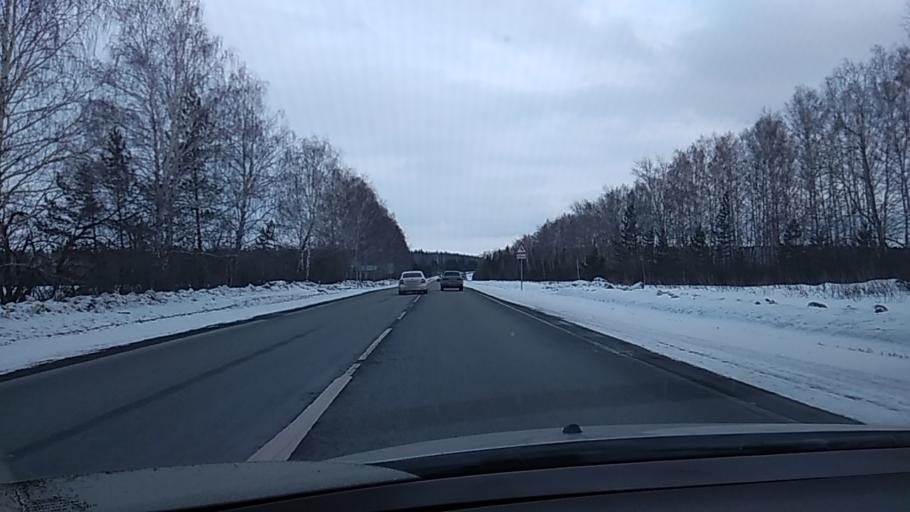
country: RU
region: Sverdlovsk
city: Sovkhoznyy
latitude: 56.5426
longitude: 61.3910
